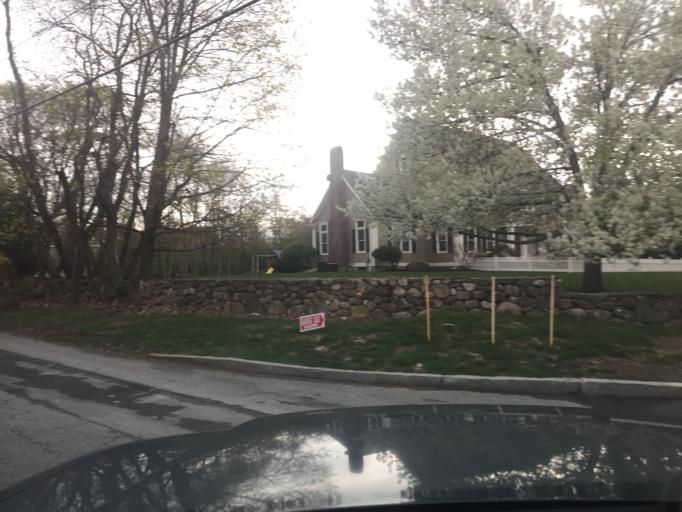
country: US
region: Massachusetts
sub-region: Norfolk County
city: Medway
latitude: 42.1600
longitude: -71.4054
